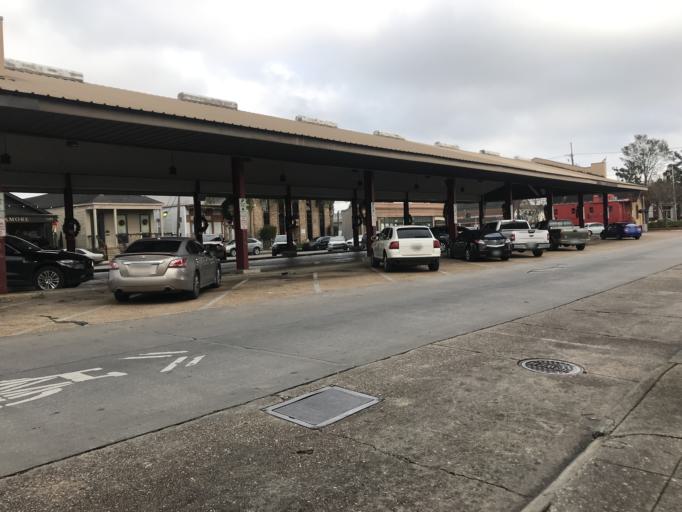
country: US
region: Louisiana
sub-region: Jefferson Parish
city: Gretna
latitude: 29.9162
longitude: -90.0654
